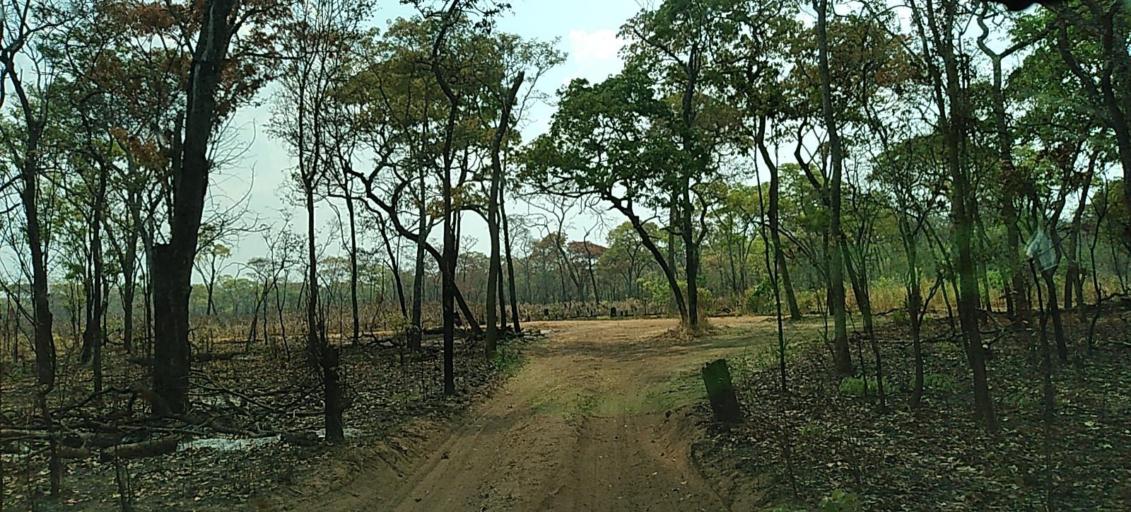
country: ZM
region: North-Western
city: Kabompo
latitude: -13.6170
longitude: 24.3706
